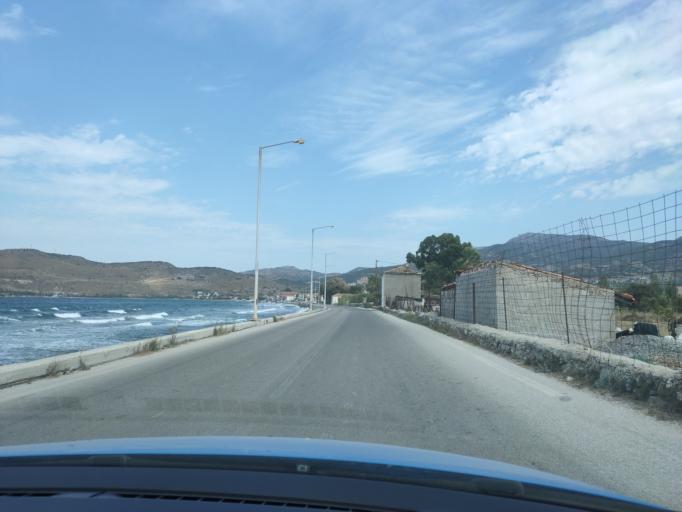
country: GR
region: North Aegean
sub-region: Nomos Lesvou
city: Petra
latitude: 39.3235
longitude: 26.1681
